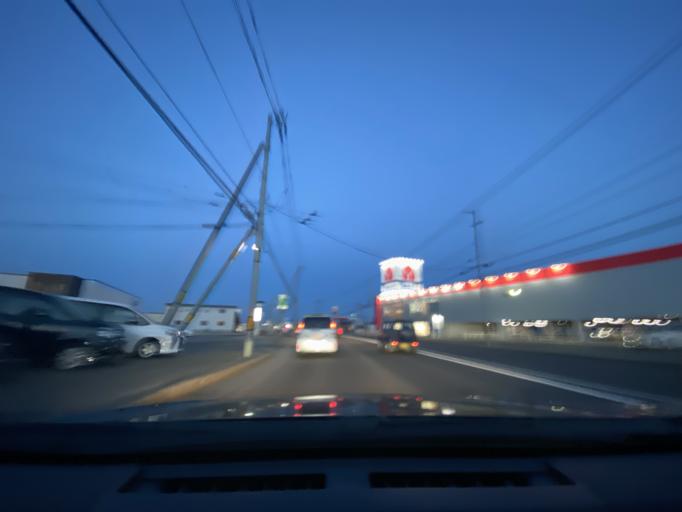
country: JP
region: Hokkaido
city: Kitami
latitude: 43.7970
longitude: 143.8378
